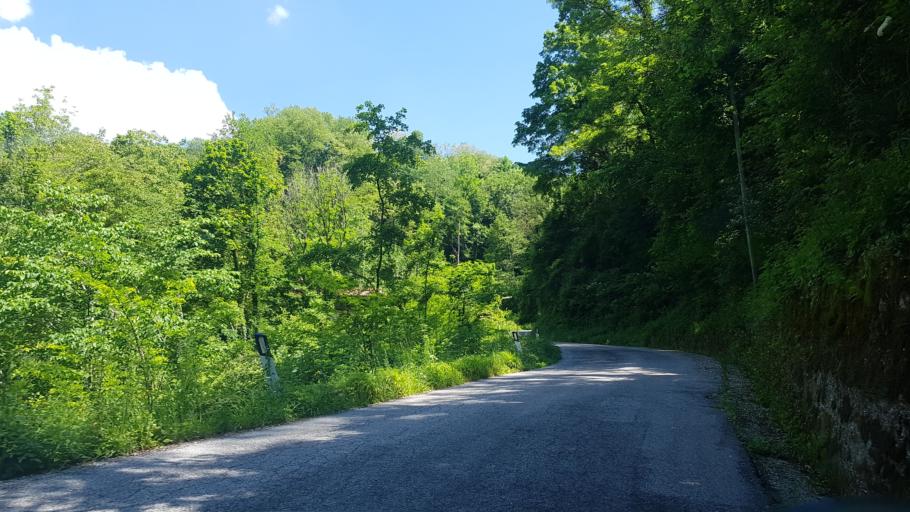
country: IT
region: Friuli Venezia Giulia
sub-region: Provincia di Udine
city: Torreano
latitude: 46.1640
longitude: 13.4304
